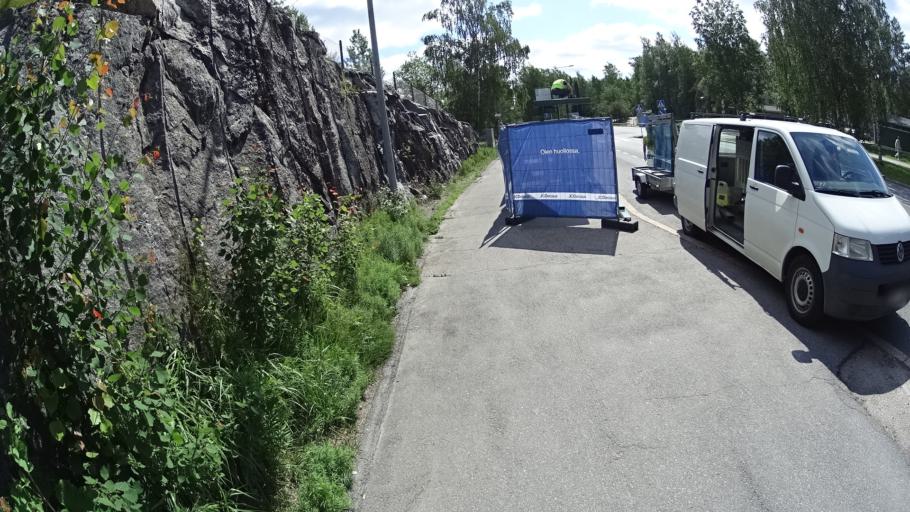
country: FI
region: Uusimaa
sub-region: Helsinki
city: Vantaa
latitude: 60.2361
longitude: 25.1265
